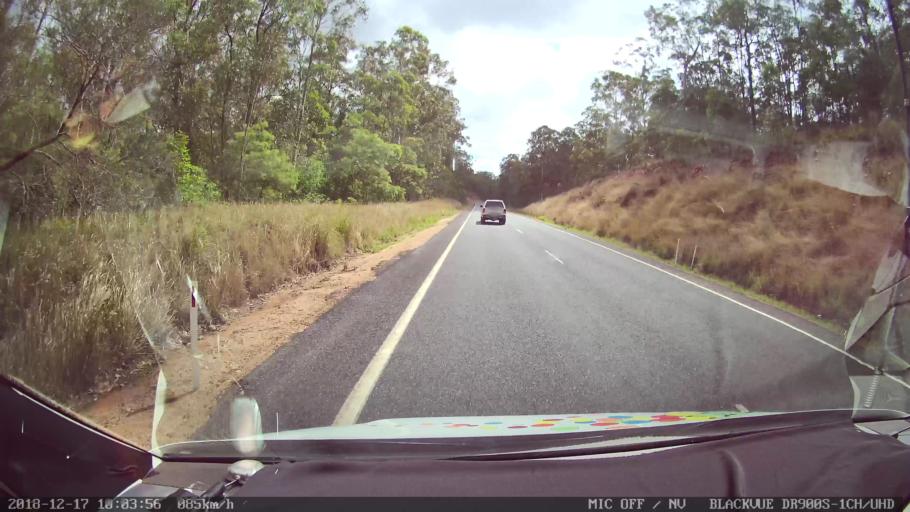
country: AU
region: New South Wales
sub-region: Tenterfield Municipality
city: Carrolls Creek
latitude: -28.8954
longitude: 152.4705
